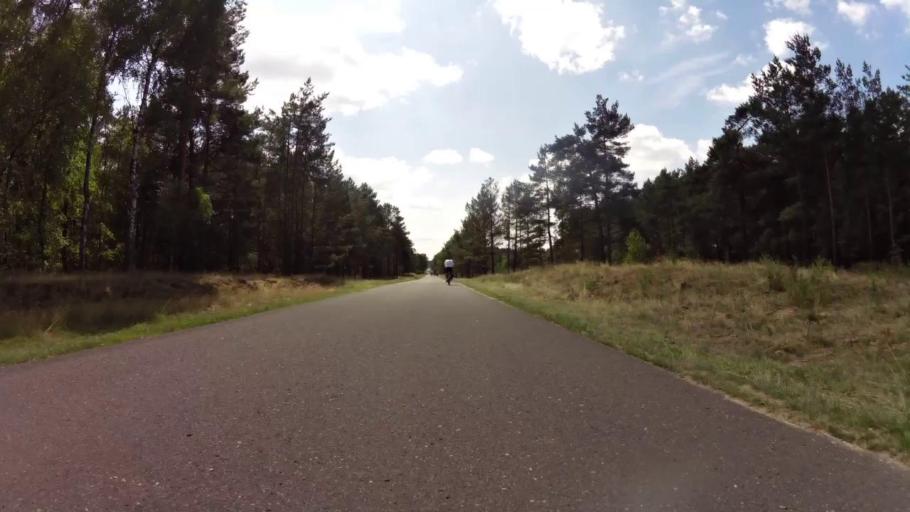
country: PL
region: West Pomeranian Voivodeship
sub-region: Powiat drawski
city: Drawsko Pomorskie
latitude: 53.4062
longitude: 15.7343
